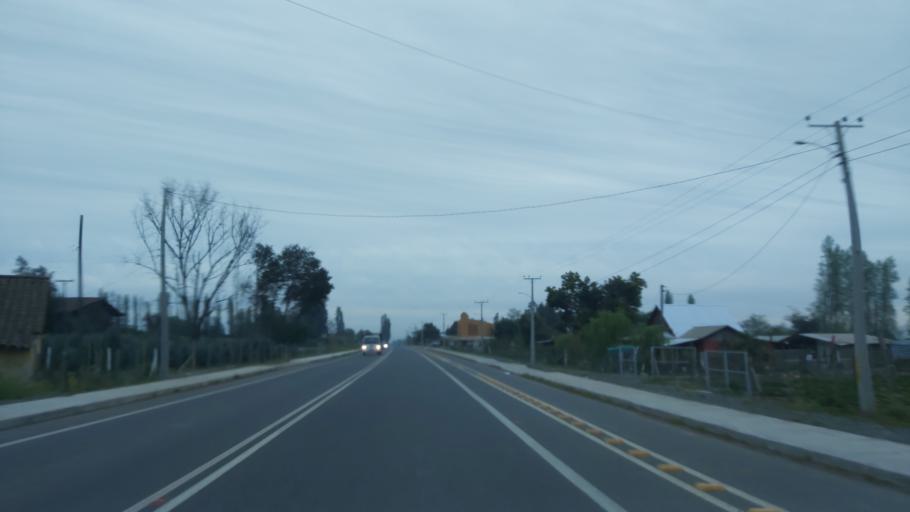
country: CL
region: Maule
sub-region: Provincia de Linares
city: Colbun
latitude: -35.6727
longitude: -71.4651
